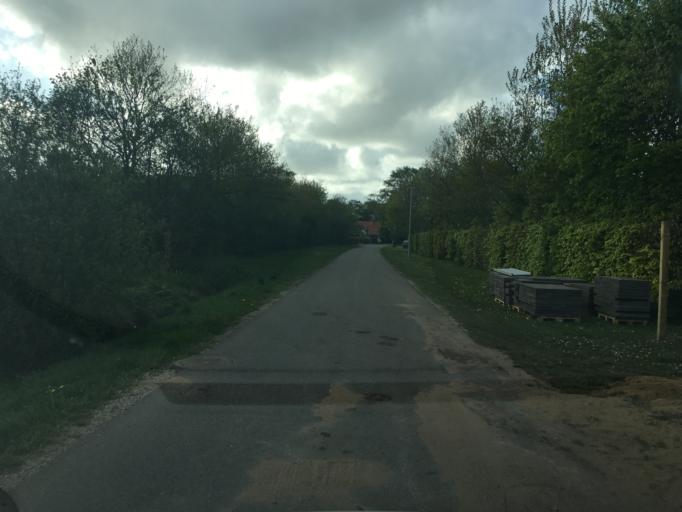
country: DE
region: Schleswig-Holstein
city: Aventoft
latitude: 55.0080
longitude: 8.7799
